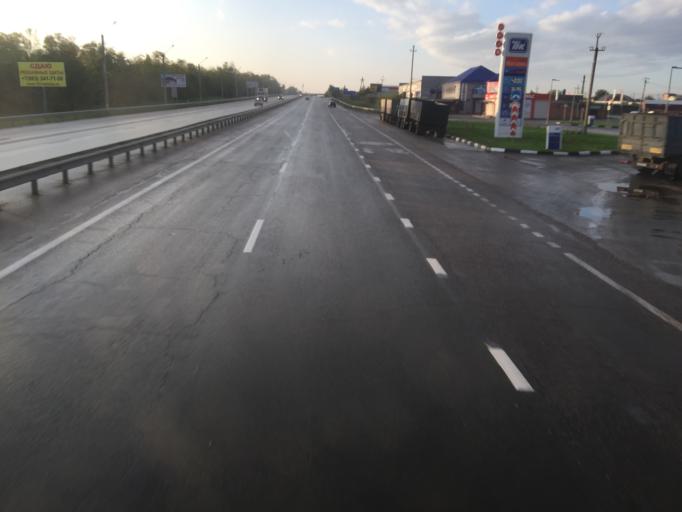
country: RU
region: Rostov
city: Bataysk
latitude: 47.0920
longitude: 39.7653
